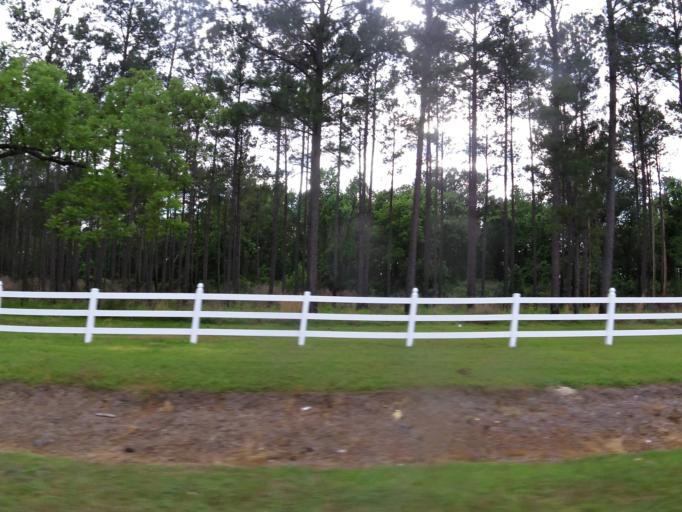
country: US
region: South Carolina
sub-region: Jasper County
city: Ridgeland
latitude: 32.4488
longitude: -81.1056
